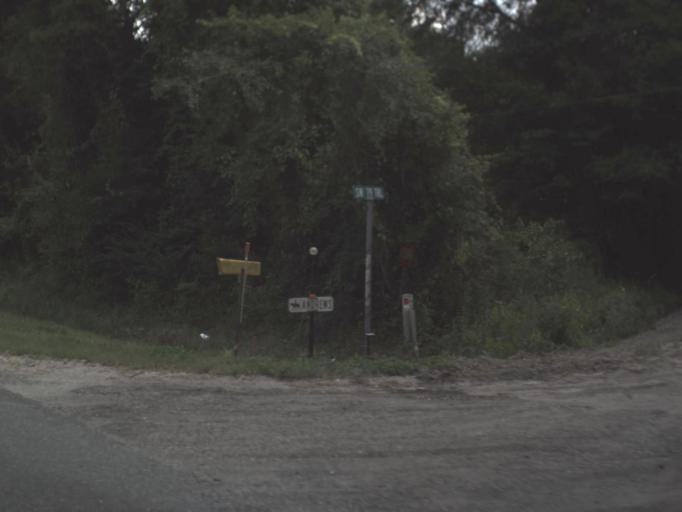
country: US
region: Florida
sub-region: Union County
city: Lake Butler
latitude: 29.9924
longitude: -82.3810
